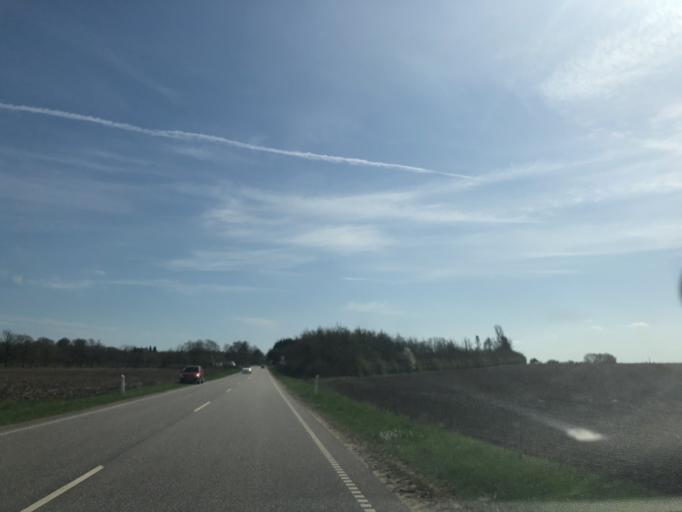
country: DK
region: Zealand
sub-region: Faxe Kommune
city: Haslev
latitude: 55.3438
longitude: 11.9405
